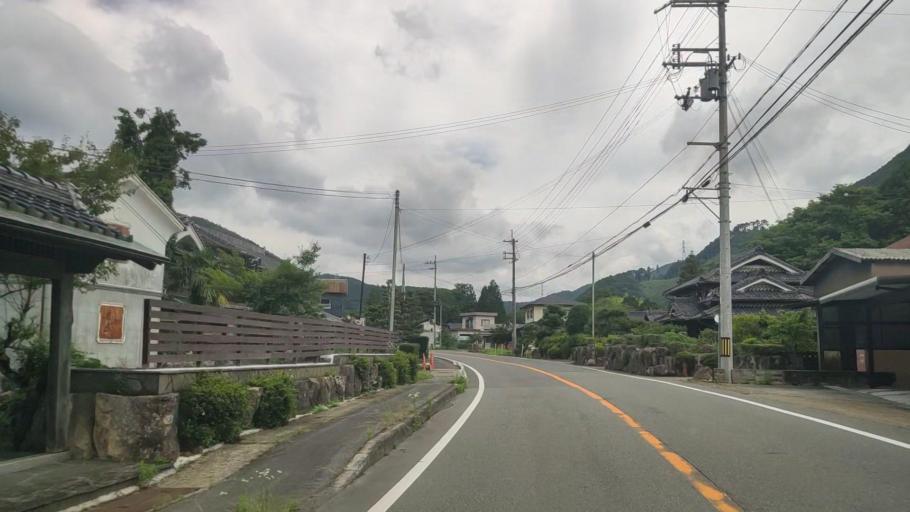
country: JP
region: Kyoto
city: Fukuchiyama
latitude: 35.2700
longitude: 134.9918
